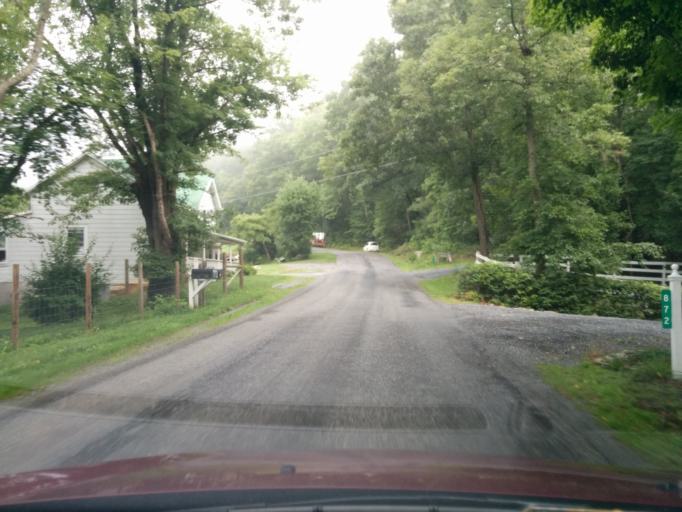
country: US
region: Virginia
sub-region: City of Lexington
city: Lexington
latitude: 37.7896
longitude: -79.4724
